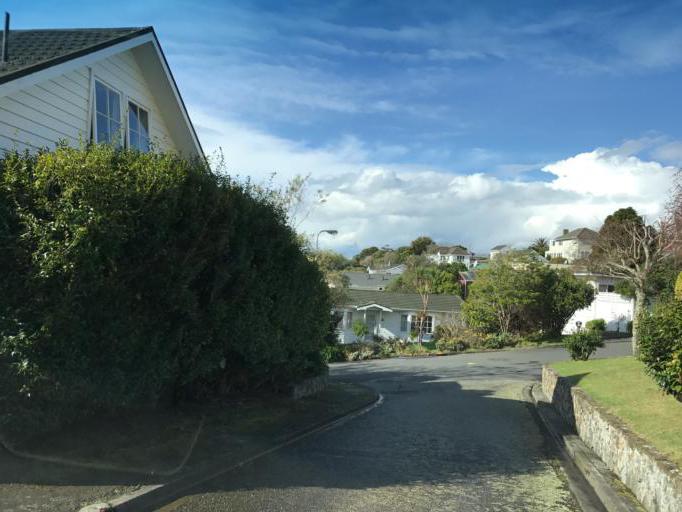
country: NZ
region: Wellington
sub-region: Wellington City
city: Kelburn
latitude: -41.2877
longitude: 174.7347
